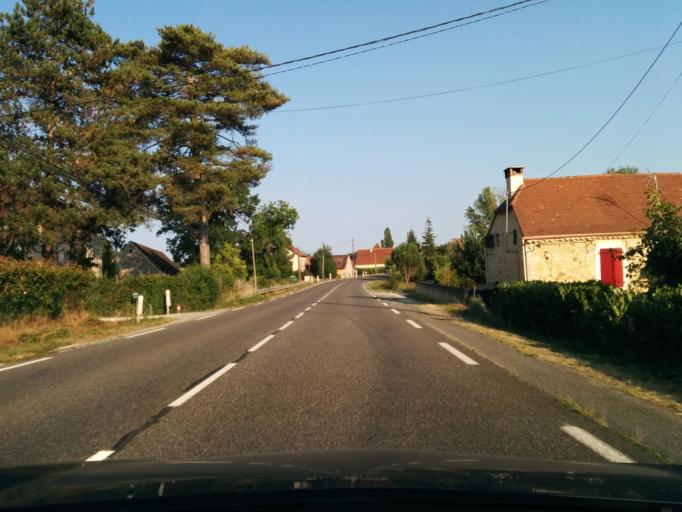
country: FR
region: Midi-Pyrenees
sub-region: Departement du Lot
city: Le Vigan
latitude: 44.7792
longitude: 1.4721
